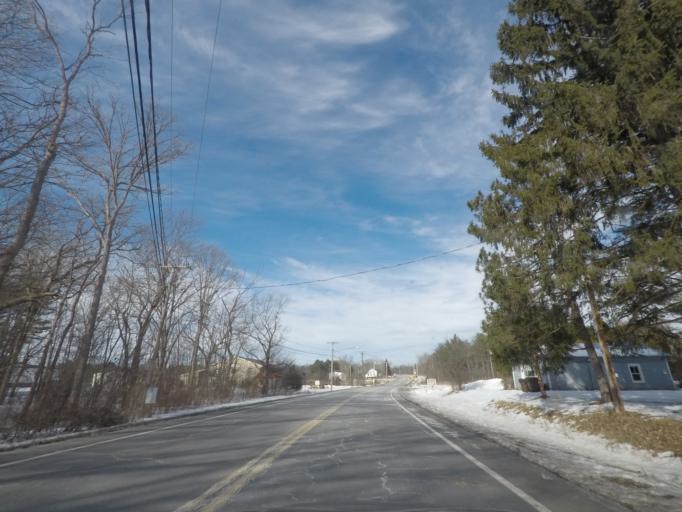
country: US
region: New York
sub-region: Albany County
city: Voorheesville
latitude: 42.6577
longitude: -73.9396
